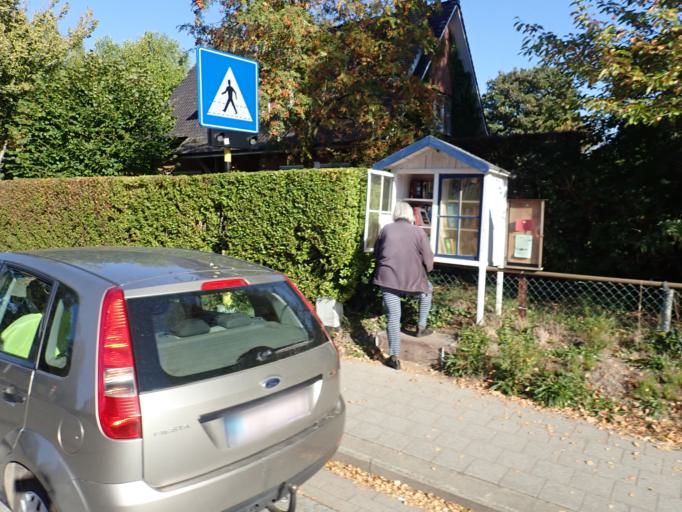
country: BE
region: Flanders
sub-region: Provincie Oost-Vlaanderen
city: Beveren
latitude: 51.2251
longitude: 4.2701
